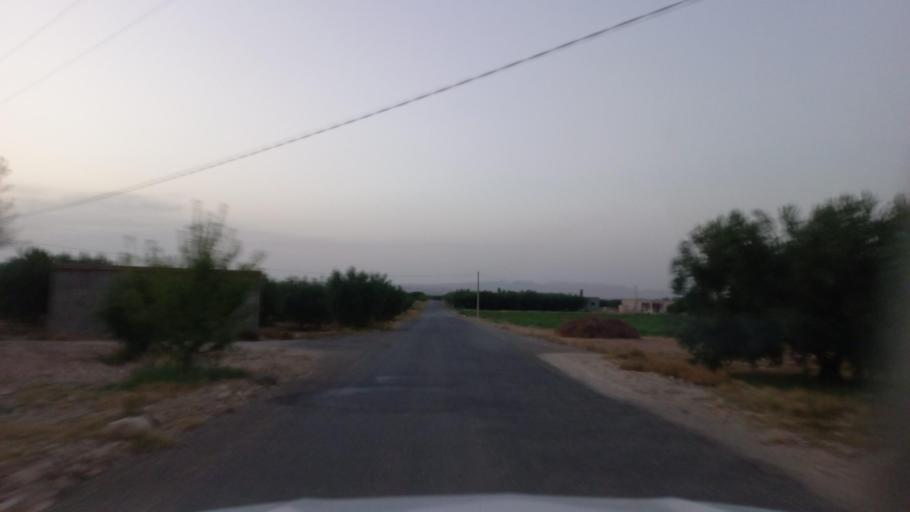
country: TN
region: Al Qasrayn
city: Kasserine
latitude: 35.2743
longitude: 9.0296
